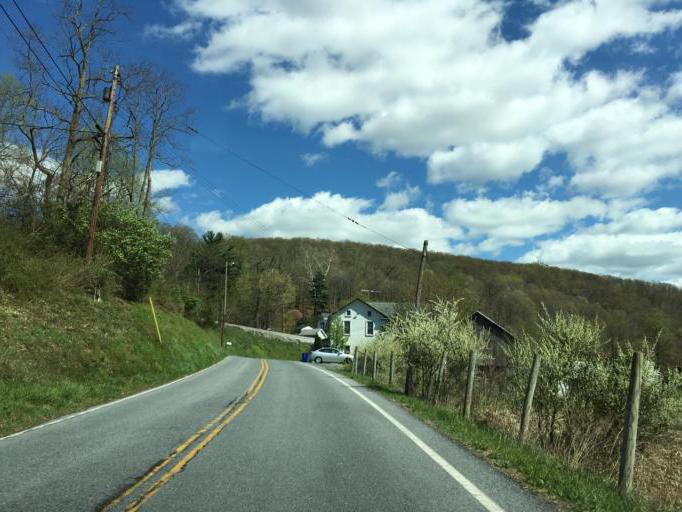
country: US
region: Maryland
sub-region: Washington County
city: Highfield-Cascade
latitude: 39.6749
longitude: -77.4569
